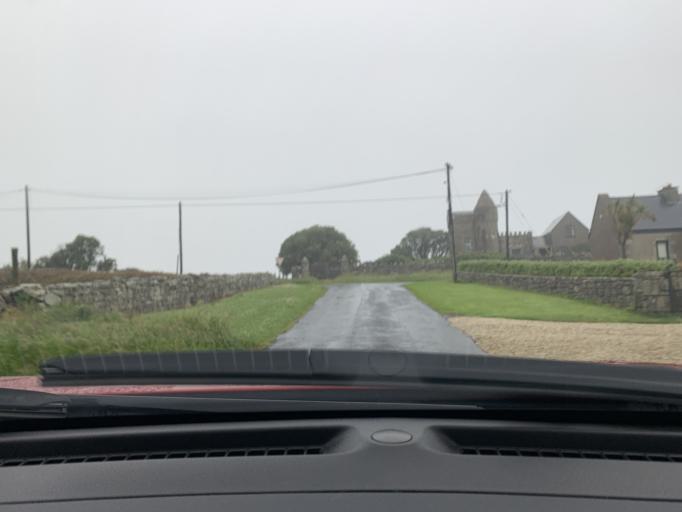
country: IE
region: Ulster
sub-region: County Donegal
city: Killybegs
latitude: 54.4690
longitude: -8.4550
